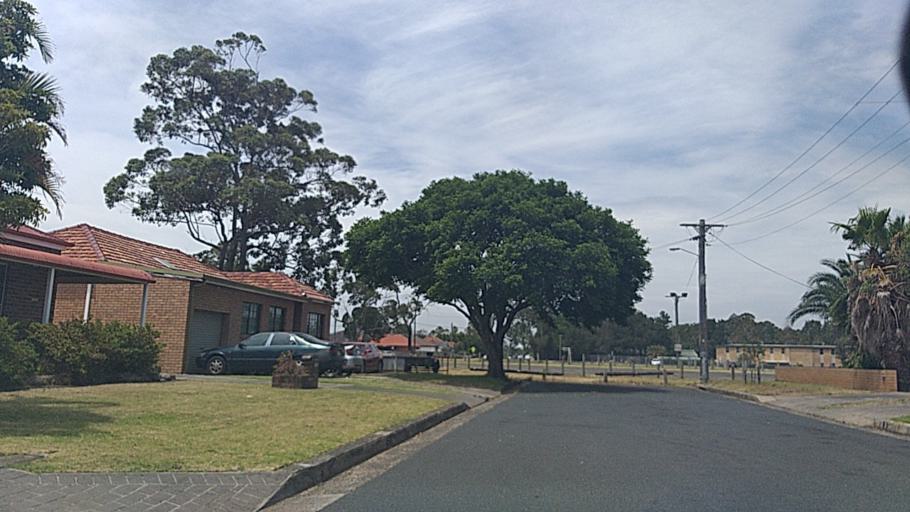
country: AU
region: New South Wales
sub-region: Wollongong
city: Fairy Meadow
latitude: -34.3895
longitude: 150.8893
